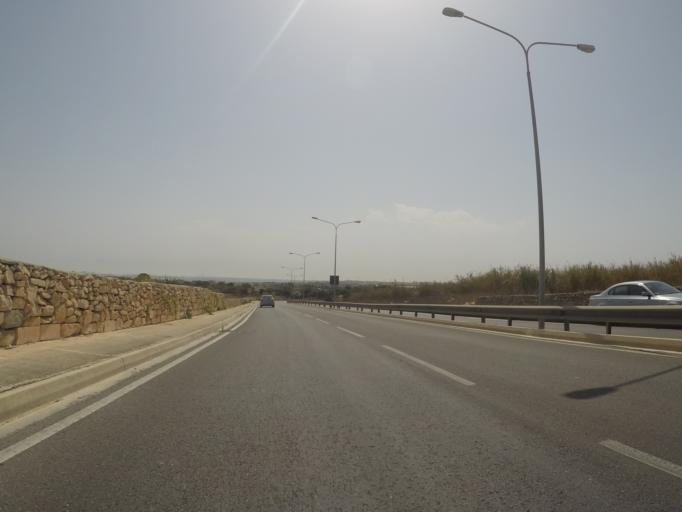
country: MT
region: L-Imdina
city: Imdina
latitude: 35.8845
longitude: 14.4133
